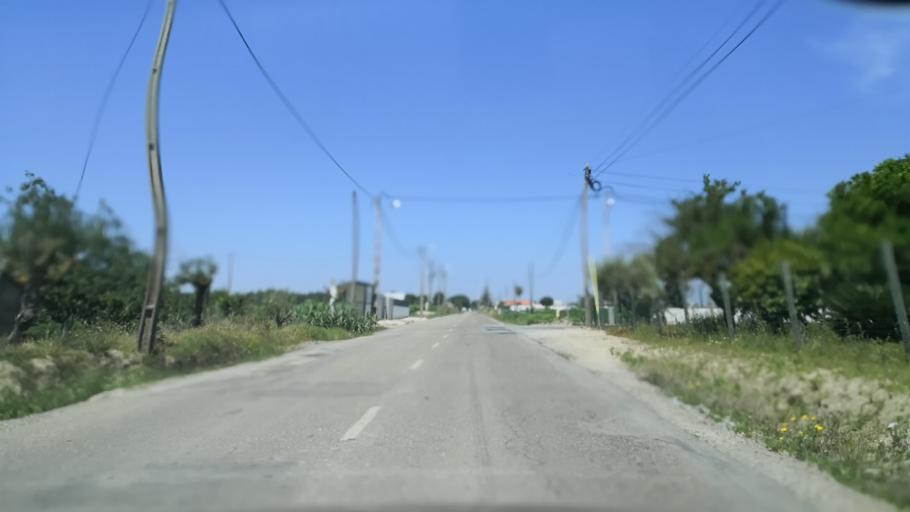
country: PT
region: Santarem
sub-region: Benavente
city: Poceirao
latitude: 38.6707
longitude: -8.7357
